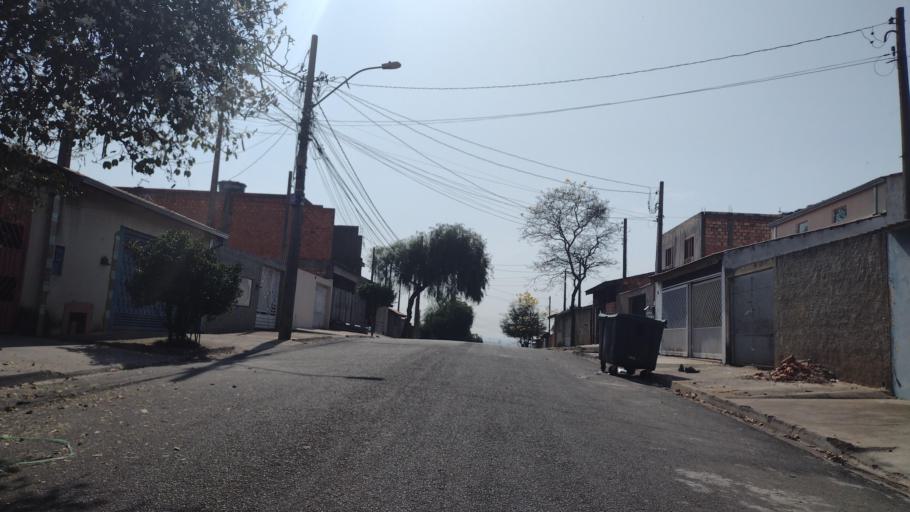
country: BR
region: Sao Paulo
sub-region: Sorocaba
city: Sorocaba
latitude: -23.4277
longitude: -47.4662
